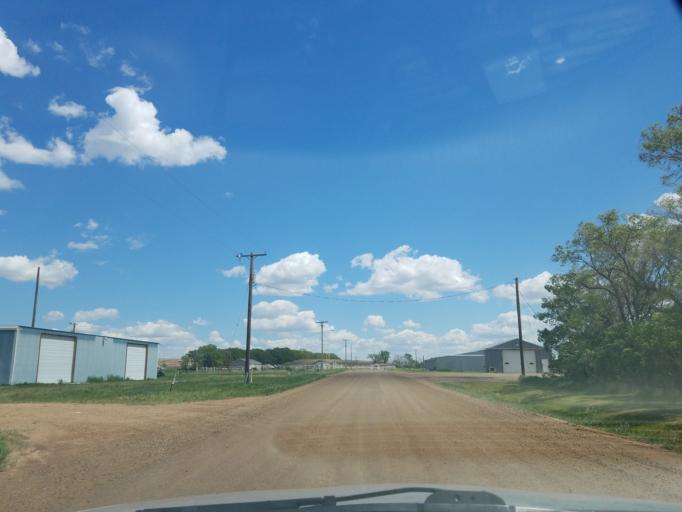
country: US
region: North Dakota
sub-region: Williams County
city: Williston
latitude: 47.8353
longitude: -103.6405
